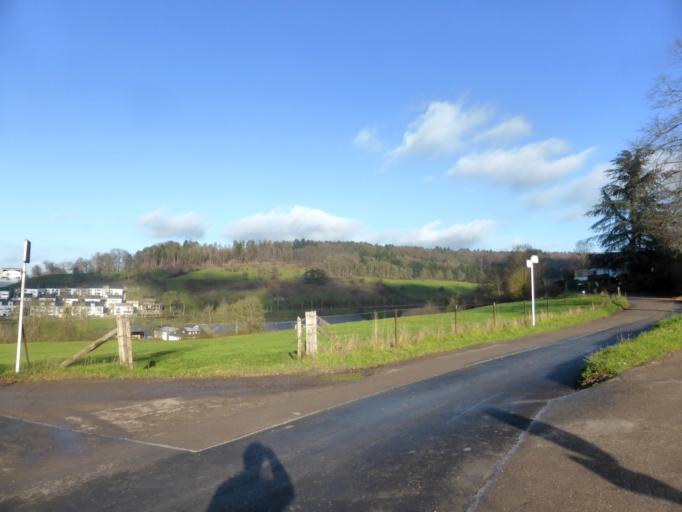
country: LU
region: Luxembourg
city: Rollingen
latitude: 49.7445
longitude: 6.1190
